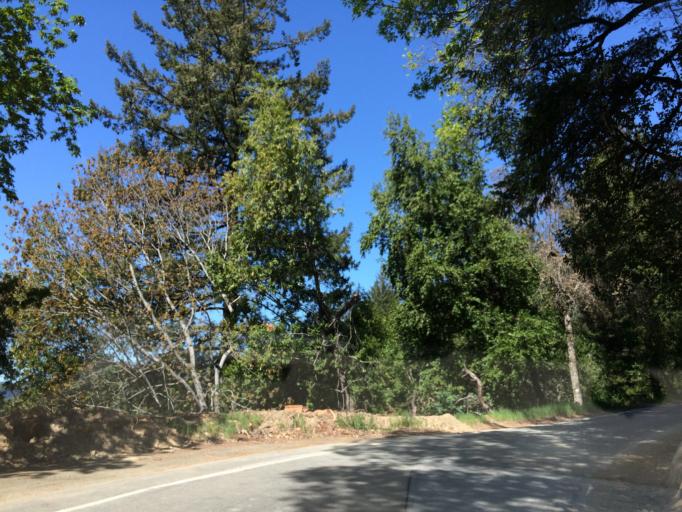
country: US
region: California
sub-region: Santa Clara County
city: Lexington Hills
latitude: 37.1680
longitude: -122.0262
